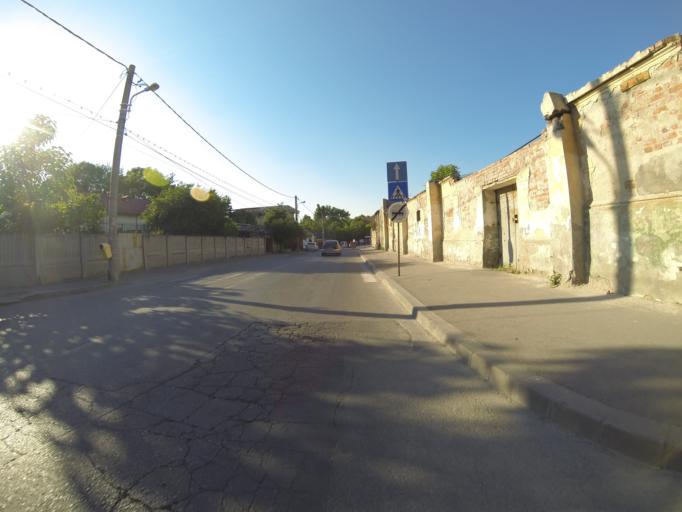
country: RO
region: Dolj
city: Craiova
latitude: 44.3071
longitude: 23.8103
